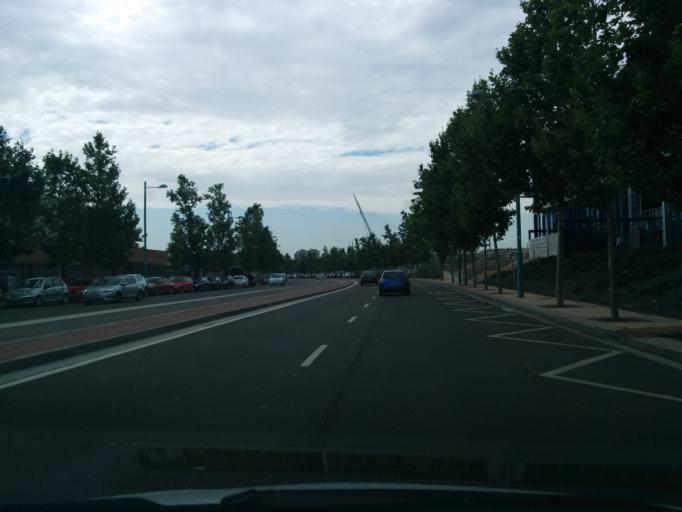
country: ES
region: Aragon
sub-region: Provincia de Zaragoza
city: Almozara
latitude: 41.6691
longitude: -0.8966
